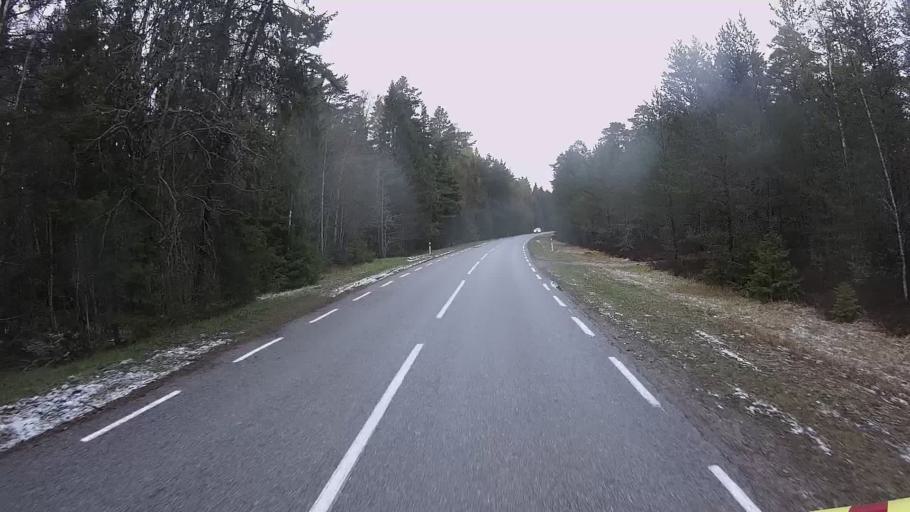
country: EE
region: Hiiumaa
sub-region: Kaerdla linn
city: Kardla
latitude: 59.0526
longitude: 22.6817
